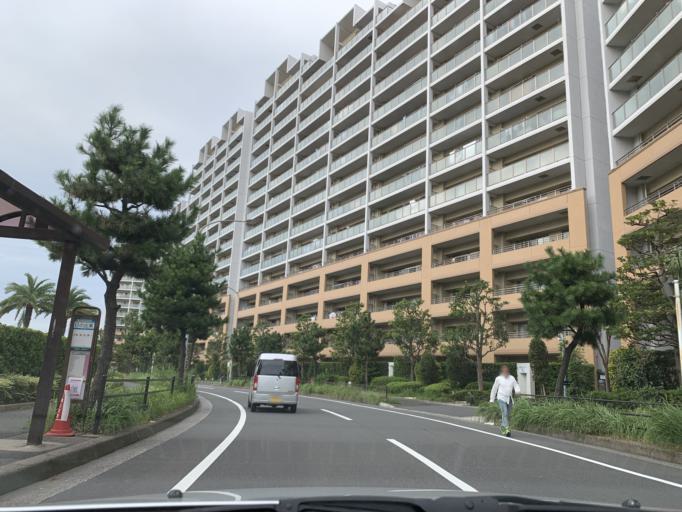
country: JP
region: Tokyo
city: Urayasu
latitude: 35.6461
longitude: 139.9300
